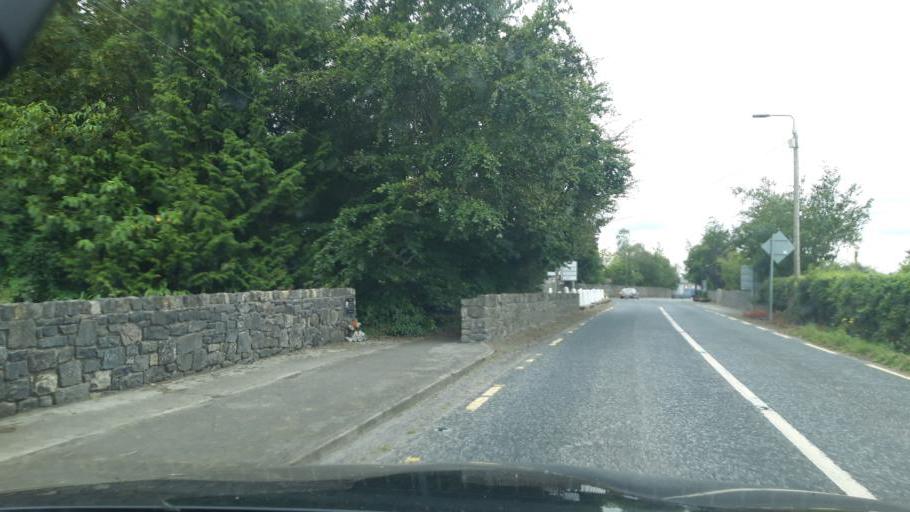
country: IE
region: Leinster
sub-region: County Carlow
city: Bagenalstown
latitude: 52.6321
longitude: -7.0600
